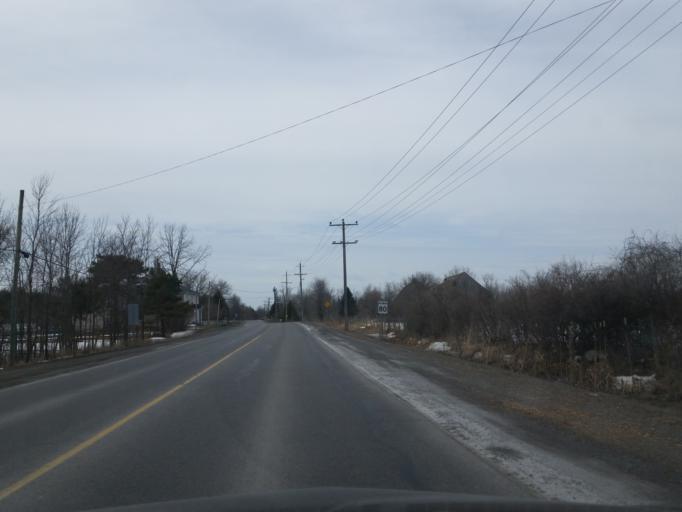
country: CA
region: Ontario
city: Skatepark
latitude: 44.2601
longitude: -76.7780
